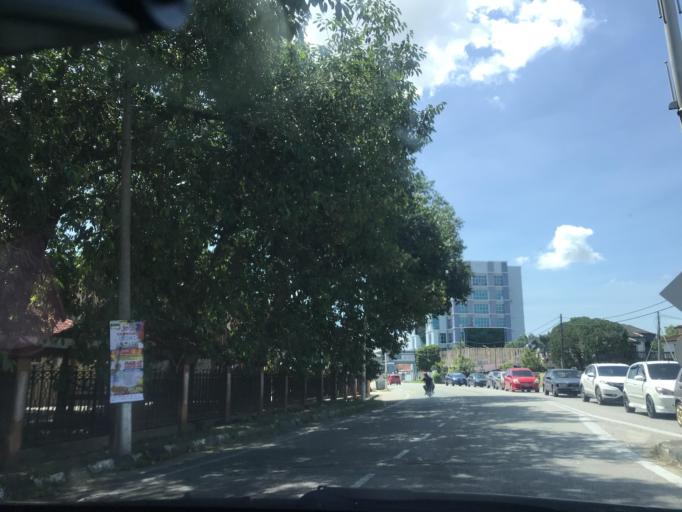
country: MY
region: Kelantan
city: Kota Bharu
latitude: 6.1094
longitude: 102.2376
